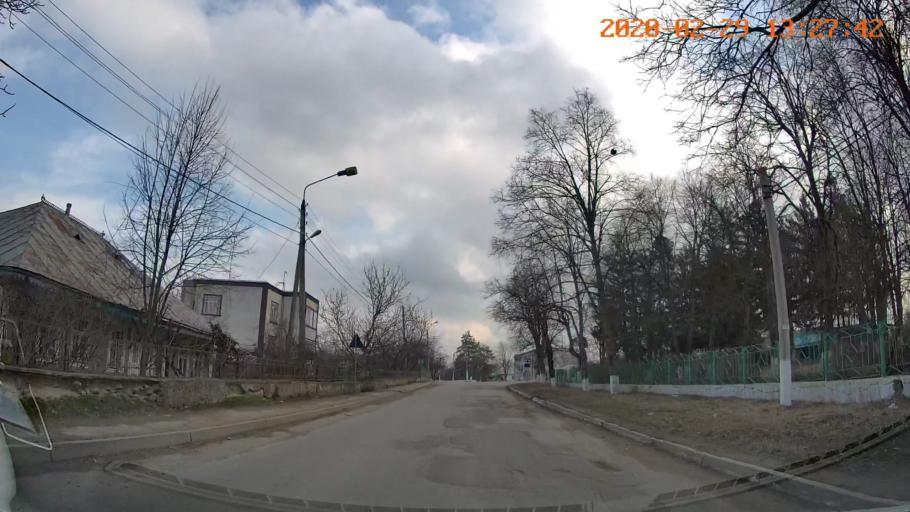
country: MD
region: Telenesti
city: Camenca
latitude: 47.9106
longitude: 28.6443
